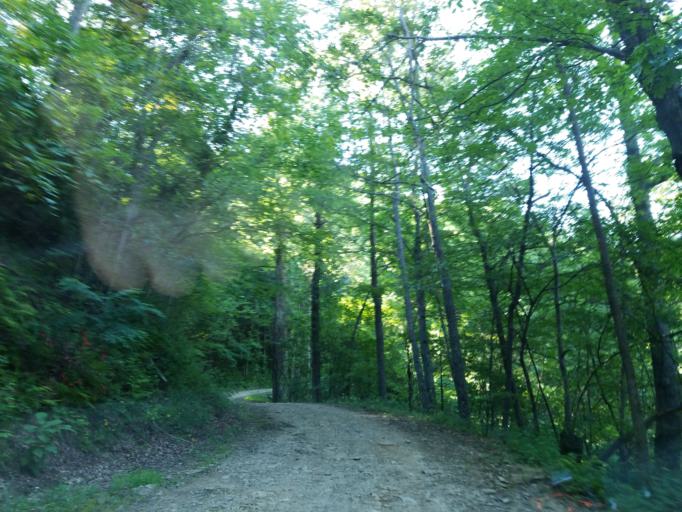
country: US
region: Georgia
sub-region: Dawson County
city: Dawsonville
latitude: 34.5971
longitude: -84.2112
